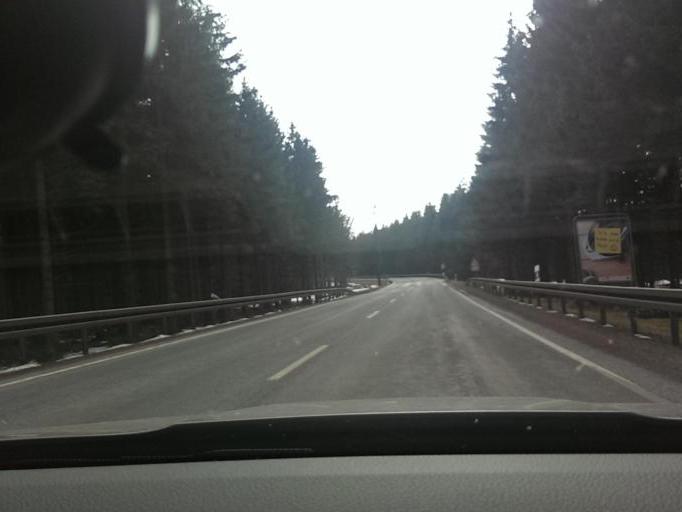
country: DE
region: Thuringia
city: Oberhof
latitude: 50.7318
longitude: 10.7287
